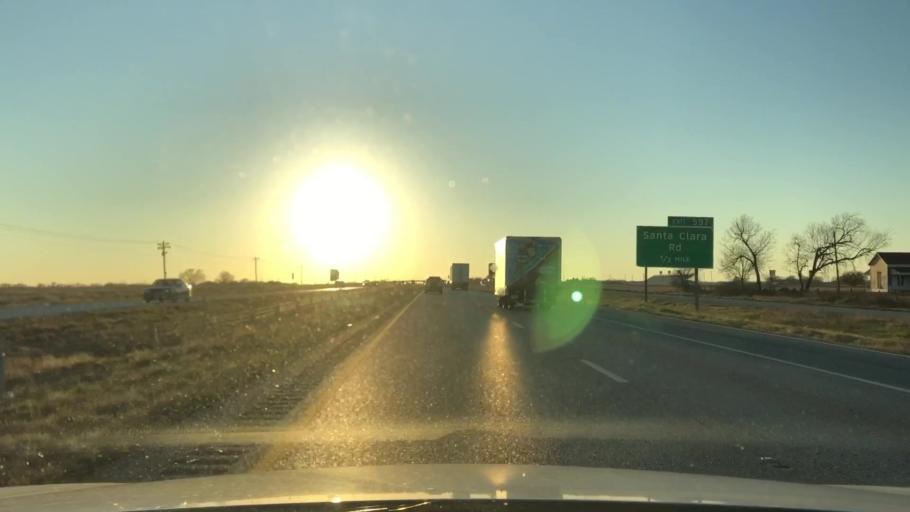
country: US
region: Texas
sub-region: Guadalupe County
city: Marion
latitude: 29.5237
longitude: -98.1270
